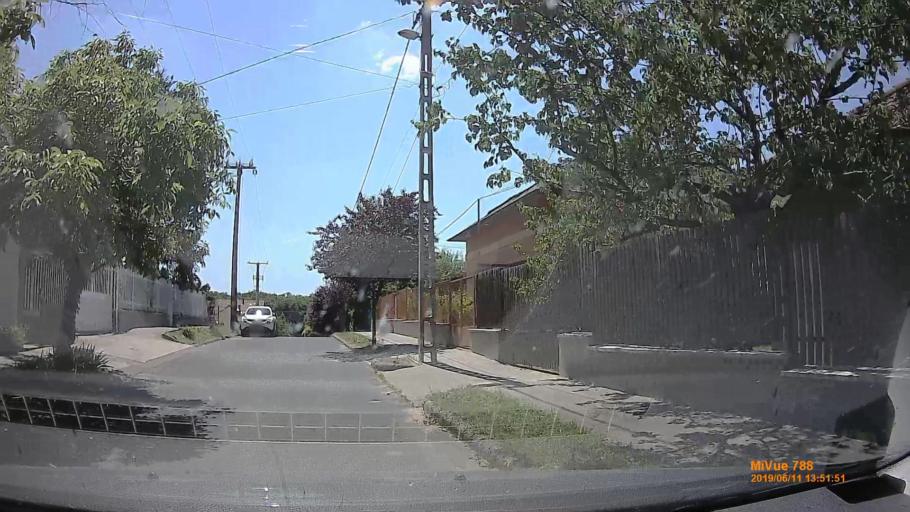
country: HU
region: Budapest
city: Budapest XXIII. keruelet
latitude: 47.3781
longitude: 19.1092
